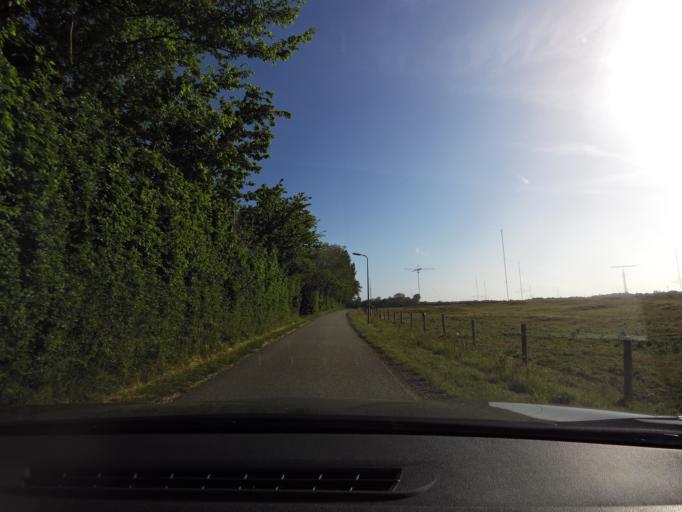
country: NL
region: South Holland
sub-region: Gemeente Goeree-Overflakkee
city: Ouddorp
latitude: 51.8066
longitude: 3.8865
